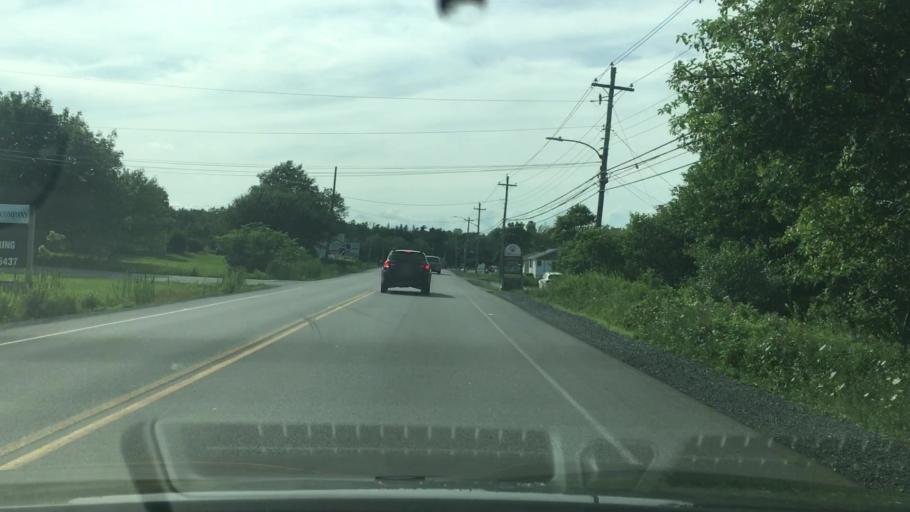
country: CA
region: Nova Scotia
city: Dartmouth
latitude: 44.7276
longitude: -63.7461
